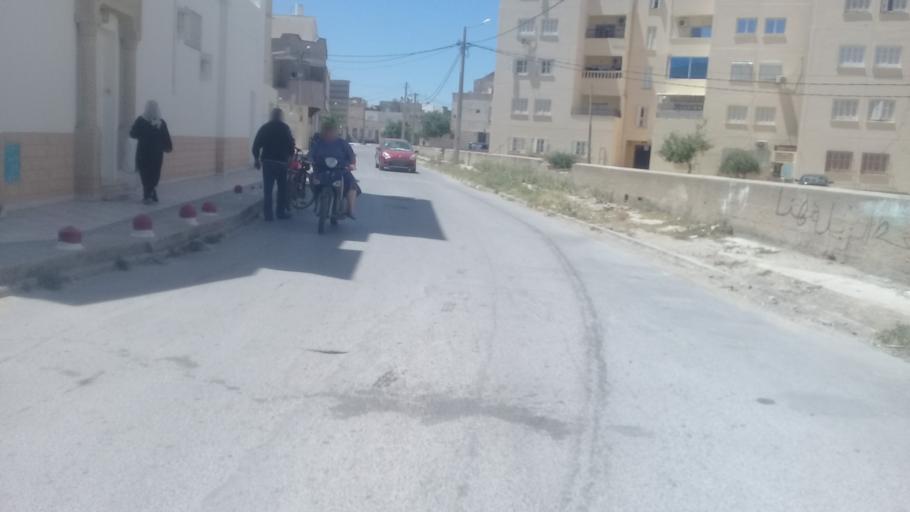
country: TN
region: Al Qayrawan
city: Kairouan
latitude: 35.6705
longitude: 10.0883
